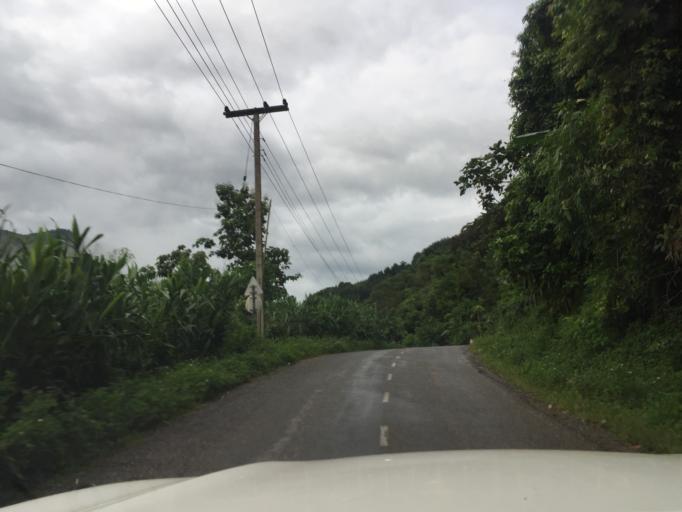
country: LA
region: Oudomxai
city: Muang La
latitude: 21.0473
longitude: 102.2411
